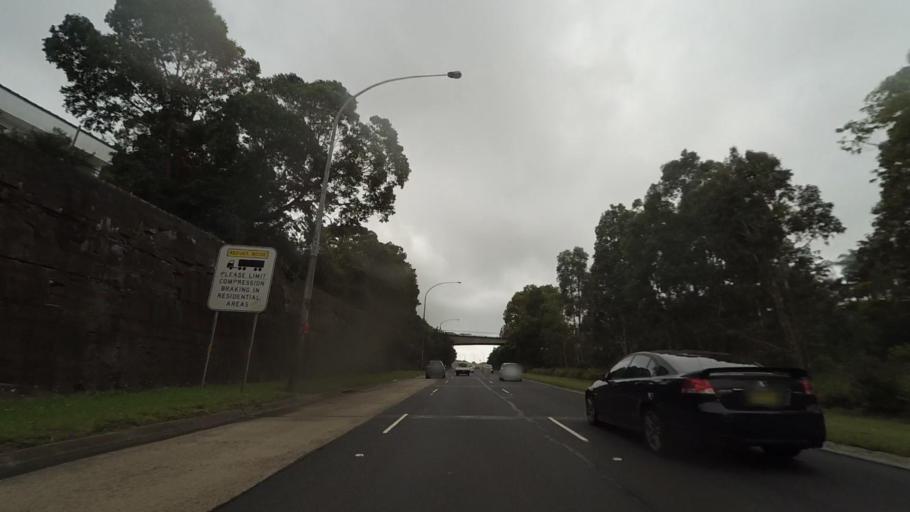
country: AU
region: New South Wales
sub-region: Kogarah
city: Blakehurst
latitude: -34.0138
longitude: 151.1245
